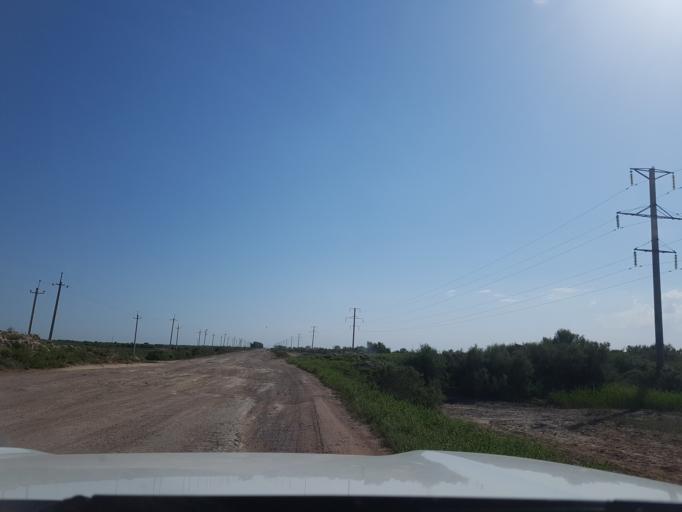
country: TM
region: Dasoguz
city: Koeneuergench
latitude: 42.1226
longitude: 58.9346
